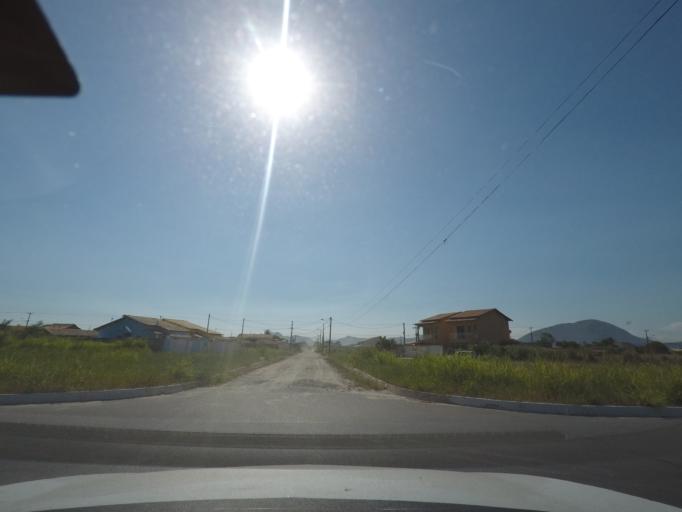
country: BR
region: Rio de Janeiro
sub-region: Marica
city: Marica
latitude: -22.9644
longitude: -42.9271
